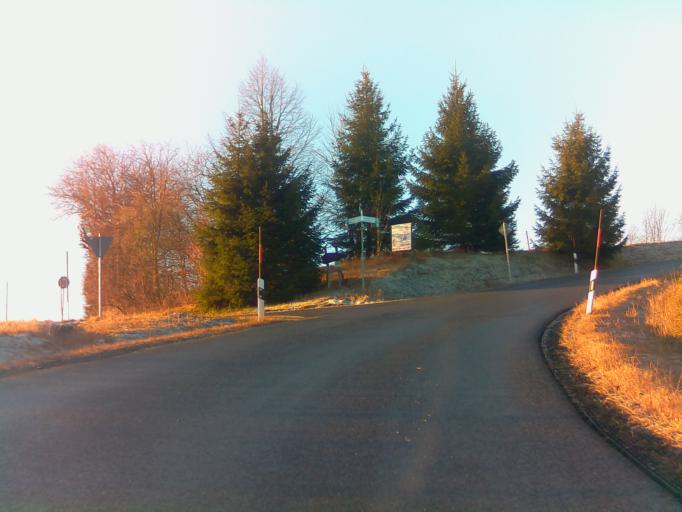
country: DE
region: Bavaria
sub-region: Upper Franconia
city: Tettau
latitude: 50.4646
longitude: 11.2566
